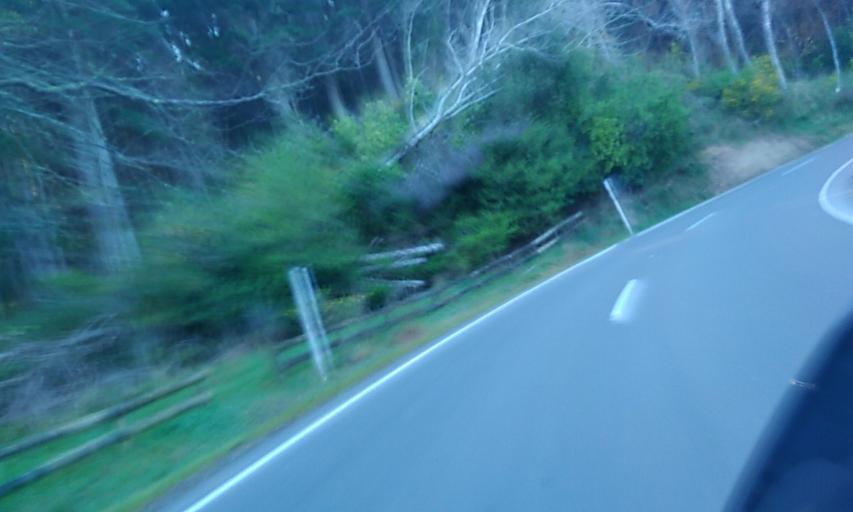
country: NZ
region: Gisborne
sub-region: Gisborne District
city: Gisborne
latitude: -38.5907
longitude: 177.9747
